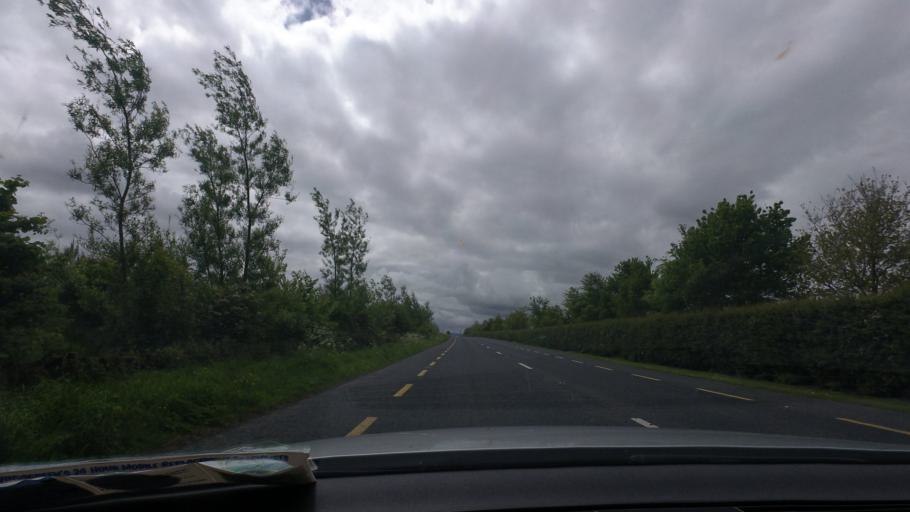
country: IE
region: Munster
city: Cashel
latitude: 52.5518
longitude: -7.8585
